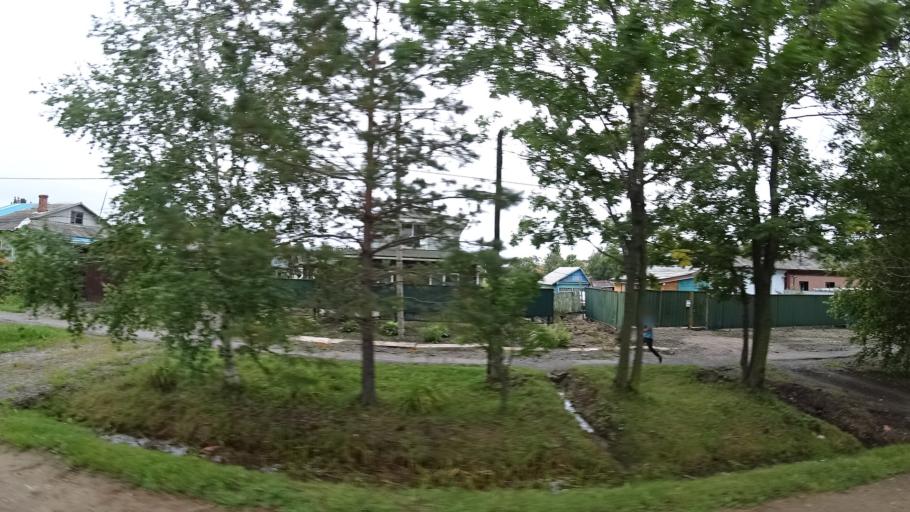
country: RU
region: Primorskiy
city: Chernigovka
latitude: 44.3399
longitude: 132.5809
